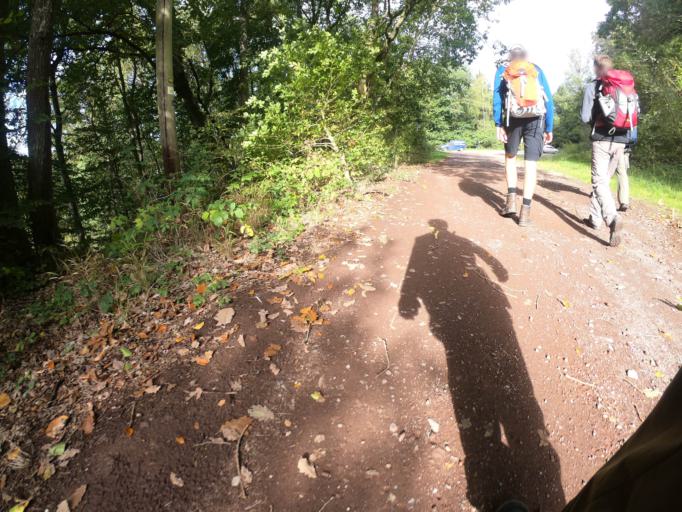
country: DE
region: Hesse
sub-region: Regierungsbezirk Darmstadt
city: Niedernhausen
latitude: 50.1275
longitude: 8.2737
